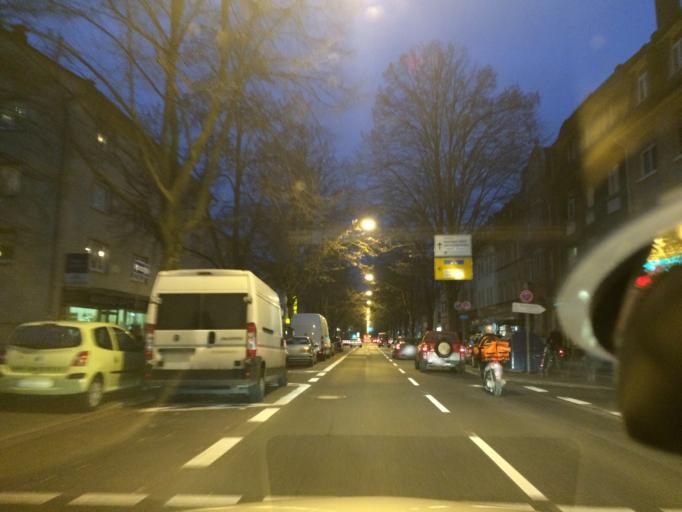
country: DE
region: Hesse
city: Sulzbach
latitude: 50.1110
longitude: 8.5381
